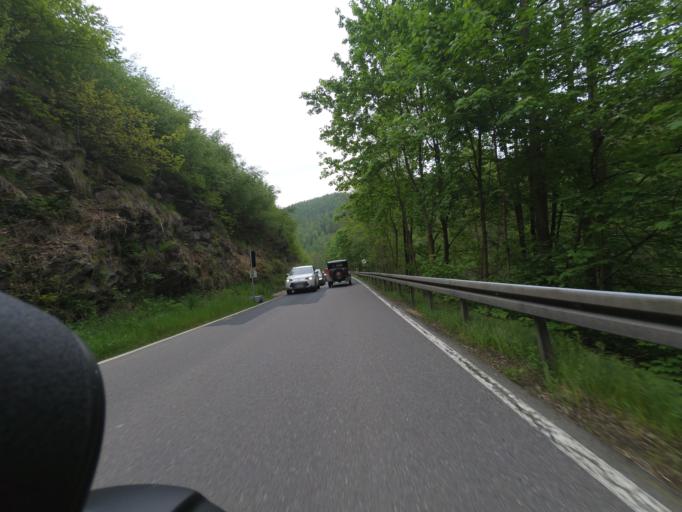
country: DE
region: Saxony
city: Scharfenstein
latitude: 50.6918
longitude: 13.0587
